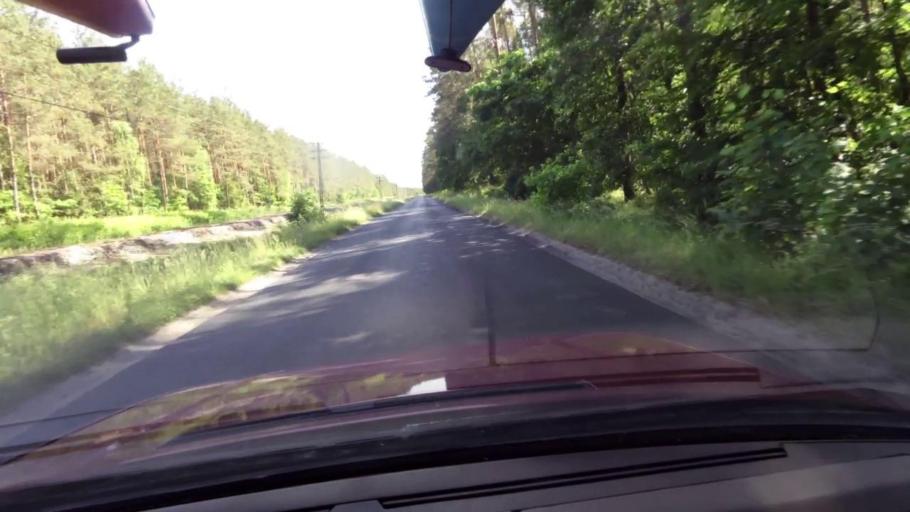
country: PL
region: Pomeranian Voivodeship
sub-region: Powiat slupski
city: Kepice
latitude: 54.2299
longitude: 16.8942
